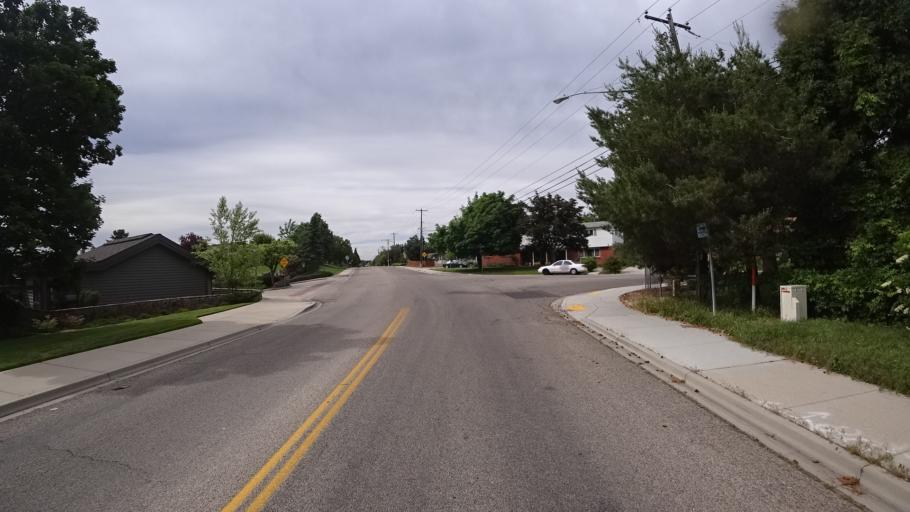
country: US
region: Idaho
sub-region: Ada County
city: Boise
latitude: 43.5776
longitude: -116.2235
